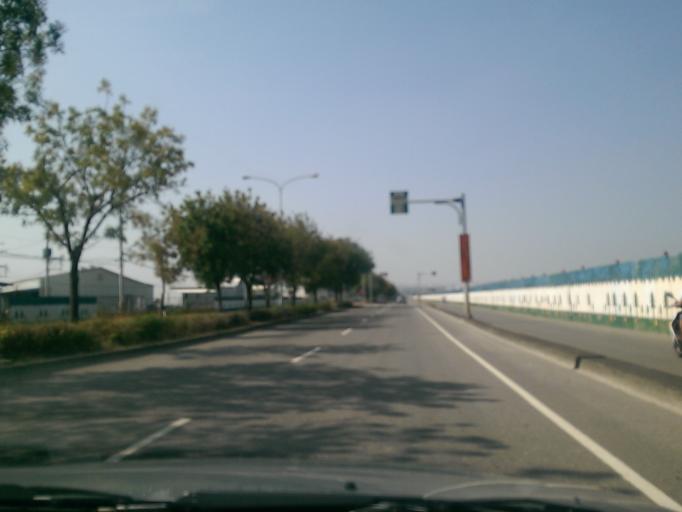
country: TW
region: Taiwan
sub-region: Taichung City
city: Taichung
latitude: 24.1204
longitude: 120.6369
